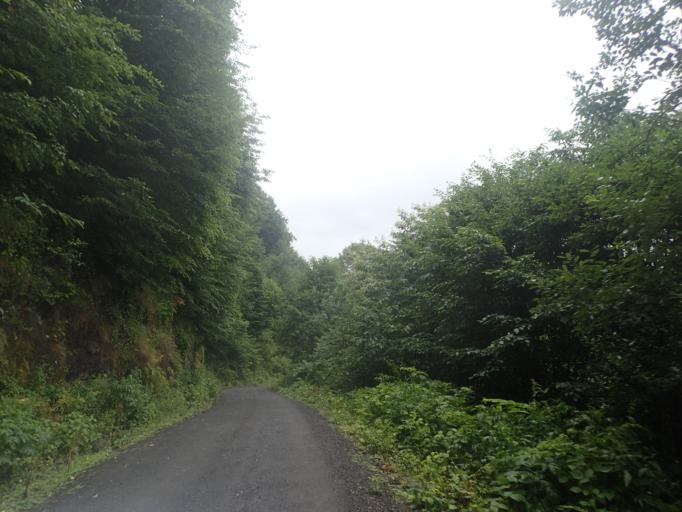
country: TR
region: Ordu
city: Akkus
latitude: 40.8931
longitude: 36.9914
